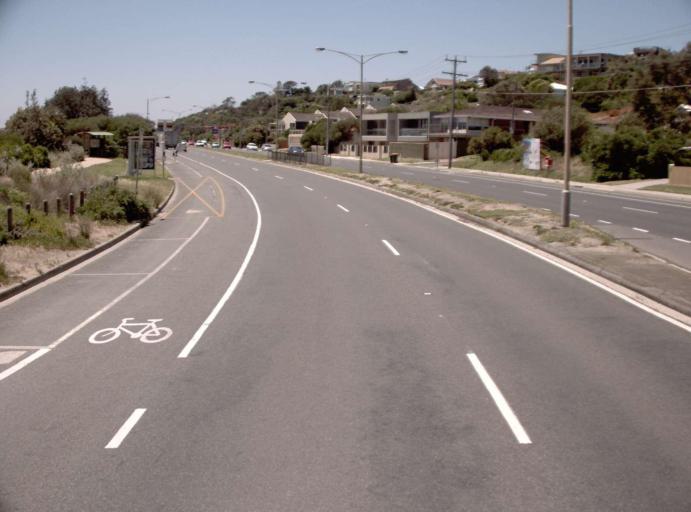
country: AU
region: Victoria
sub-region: Frankston
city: Frankston
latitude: -38.1523
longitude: 145.1124
